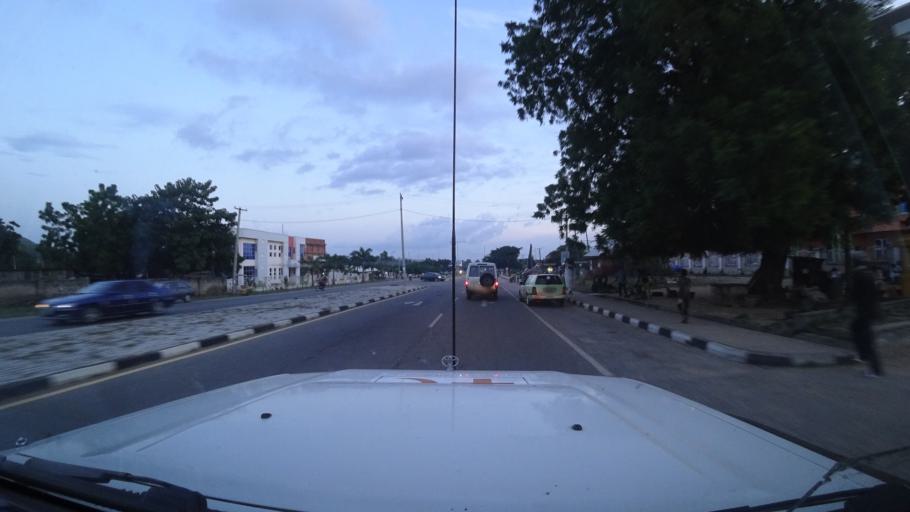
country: NG
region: Niger
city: Minna
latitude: 9.6367
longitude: 6.5425
